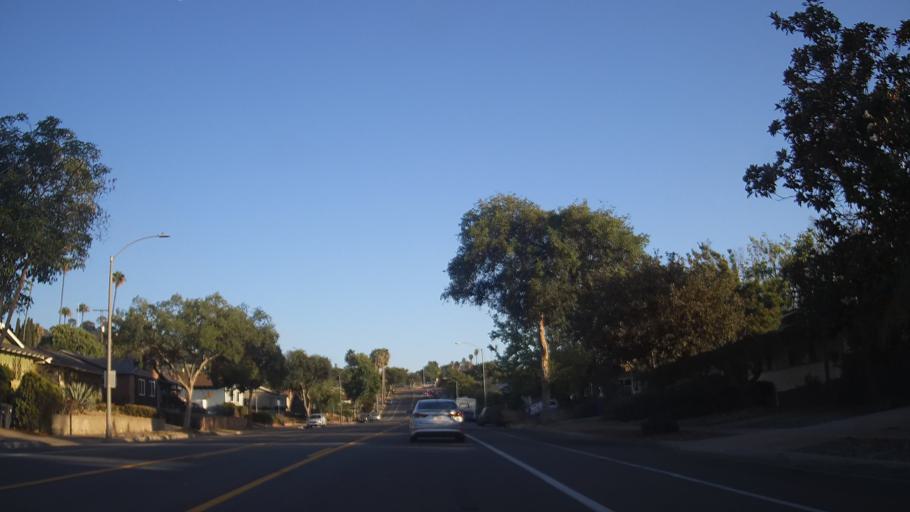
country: US
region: California
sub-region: San Diego County
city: La Mesa
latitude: 32.7834
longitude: -116.9978
